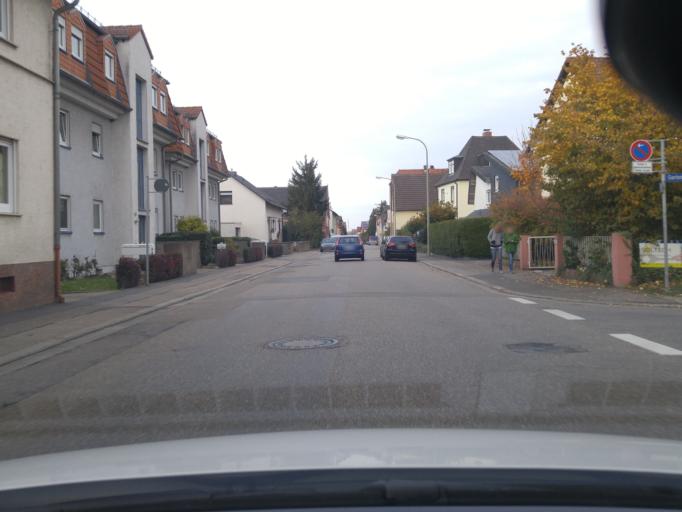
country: DE
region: Rheinland-Pfalz
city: Dudenhofen
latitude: 49.2929
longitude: 8.4047
